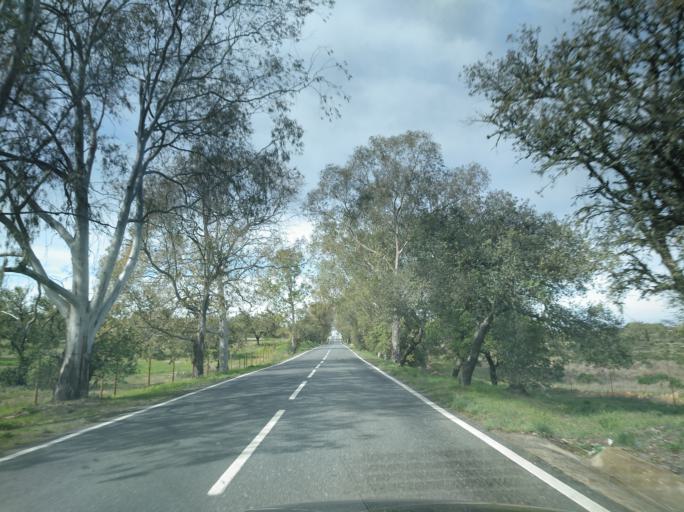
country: PT
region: Beja
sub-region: Mertola
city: Mertola
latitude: 37.7332
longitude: -7.7705
